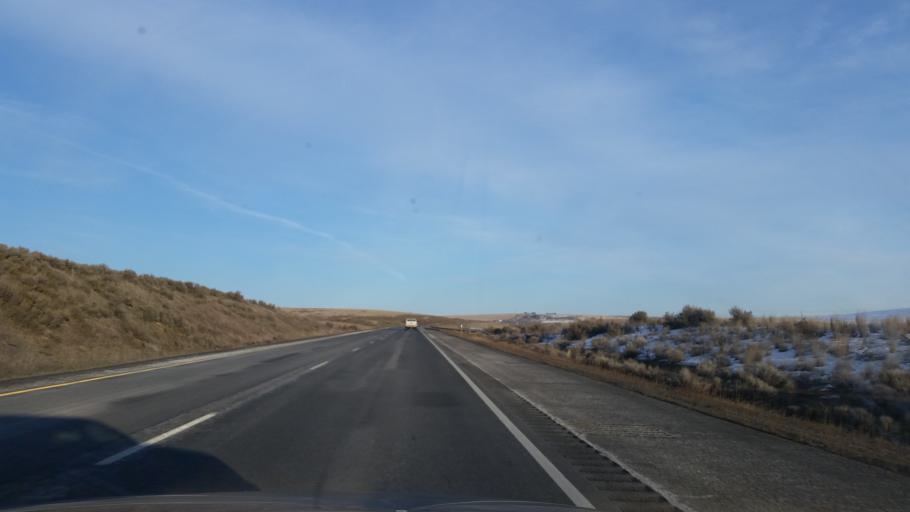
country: US
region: Washington
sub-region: Grant County
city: Warden
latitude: 47.0867
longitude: -118.9319
